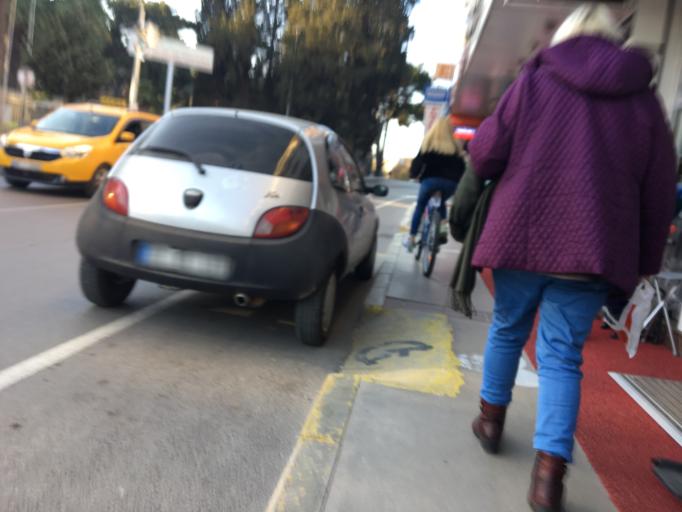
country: TR
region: Izmir
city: Buca
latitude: 38.3852
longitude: 27.1664
